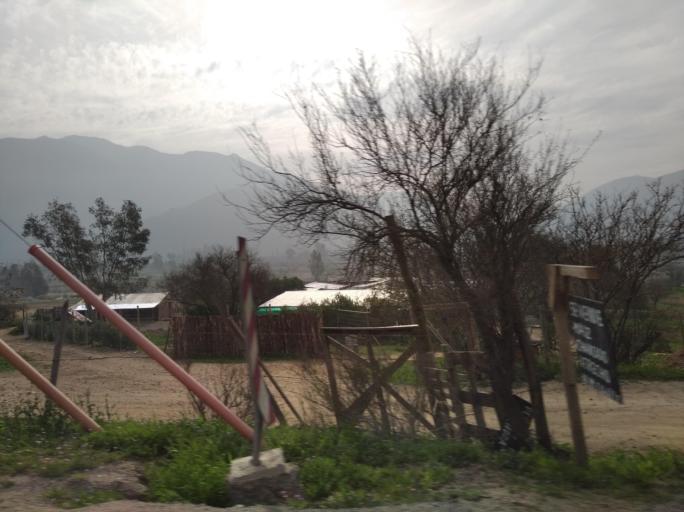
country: CL
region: Santiago Metropolitan
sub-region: Provincia de Chacabuco
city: Lampa
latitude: -33.2602
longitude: -70.8991
